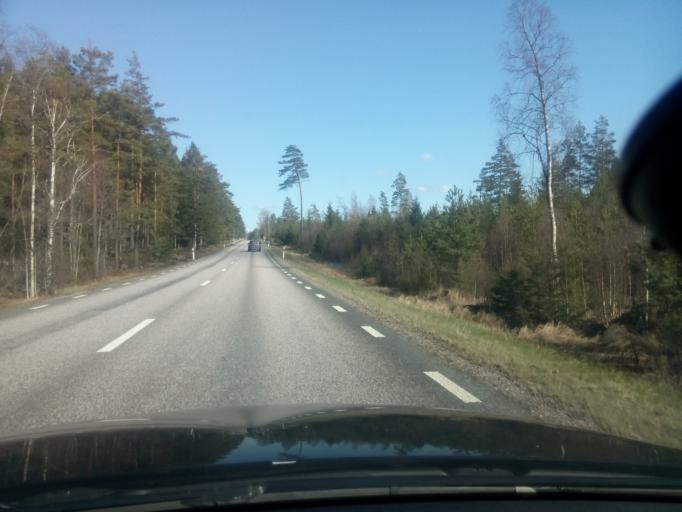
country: SE
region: Soedermanland
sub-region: Flens Kommun
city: Malmkoping
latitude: 59.2059
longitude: 16.8071
